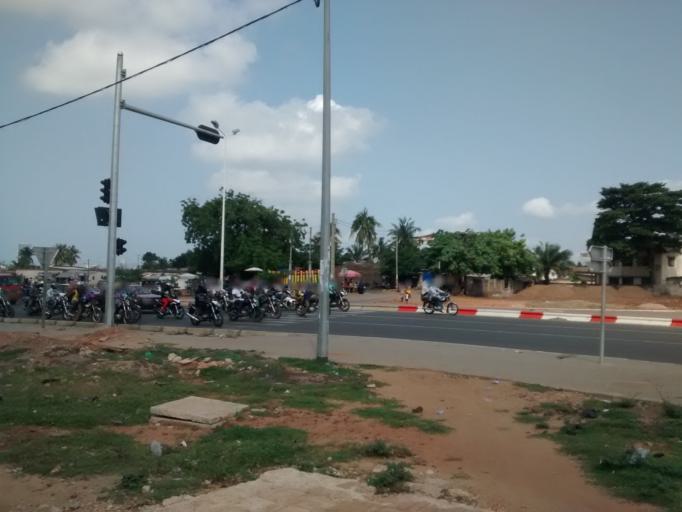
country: TG
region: Maritime
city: Lome
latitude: 6.1492
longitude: 1.2303
